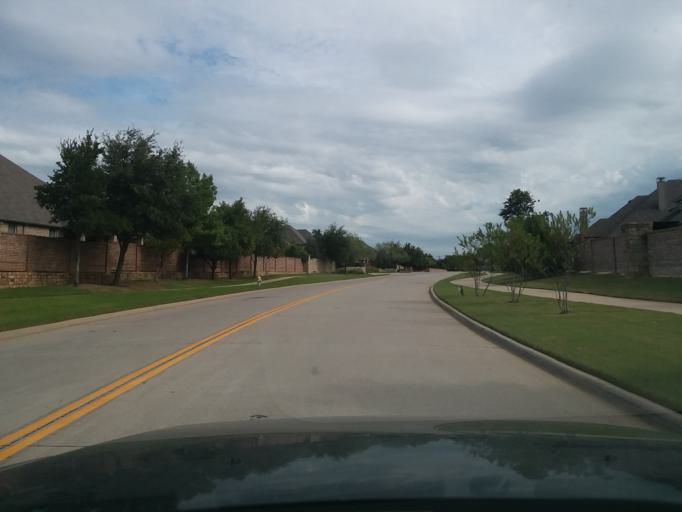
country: US
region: Texas
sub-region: Denton County
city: Copper Canyon
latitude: 33.1111
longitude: -97.1230
